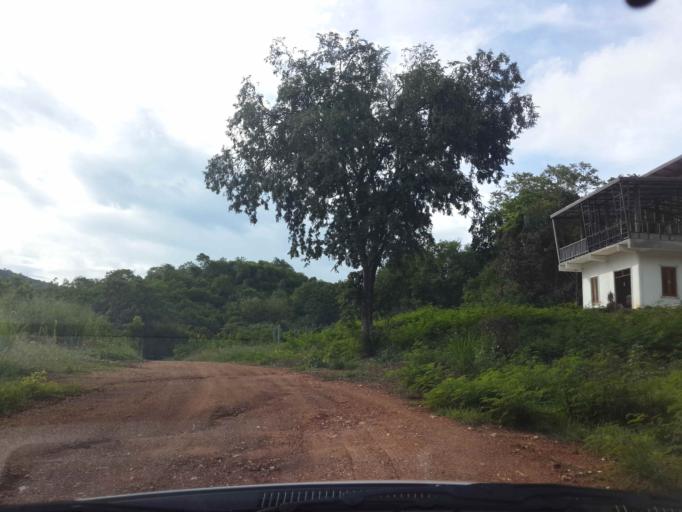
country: TH
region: Kanchanaburi
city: Dan Makham Tia
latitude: 13.7541
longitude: 99.2028
